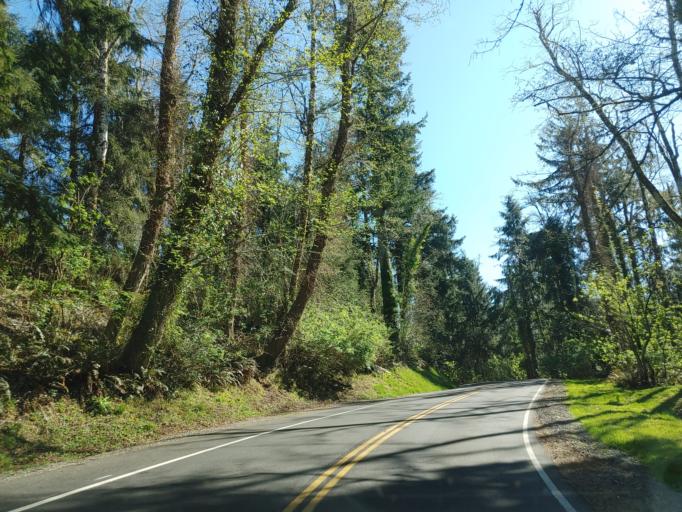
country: US
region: Oregon
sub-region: Clatsop County
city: Astoria
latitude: 46.1819
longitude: -123.8238
